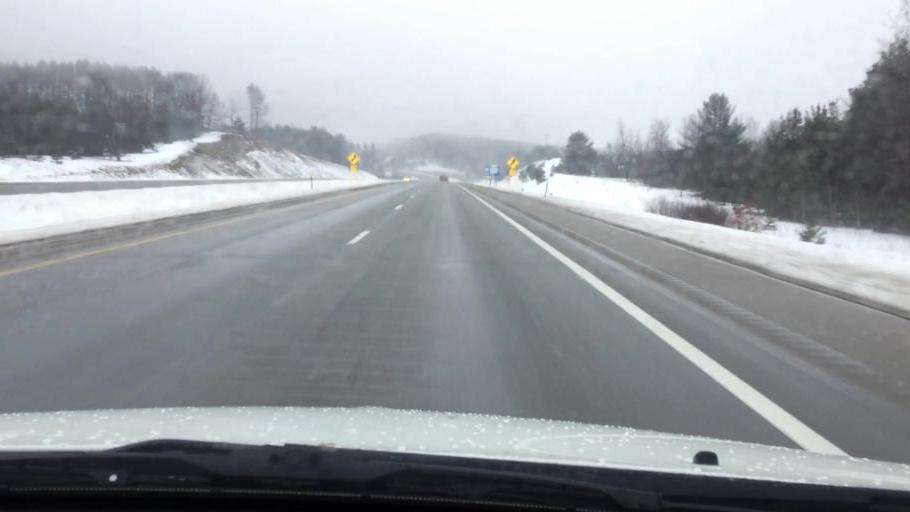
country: US
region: Michigan
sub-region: Wexford County
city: Cadillac
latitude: 44.3061
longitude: -85.3924
